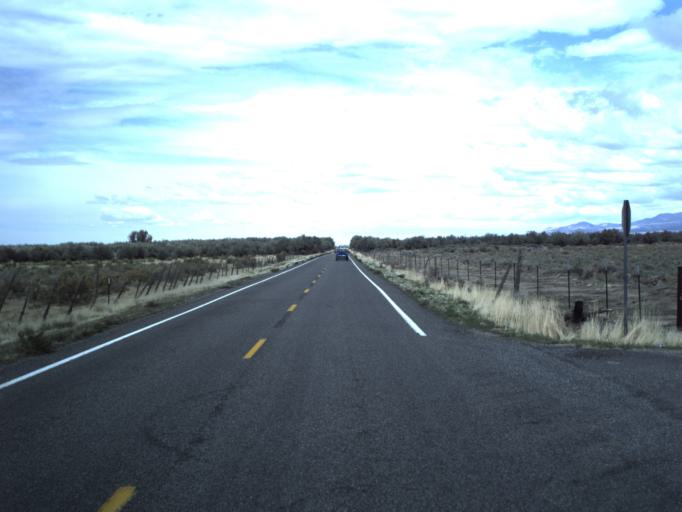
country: US
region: Utah
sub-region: Millard County
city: Fillmore
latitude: 39.0812
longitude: -112.4099
